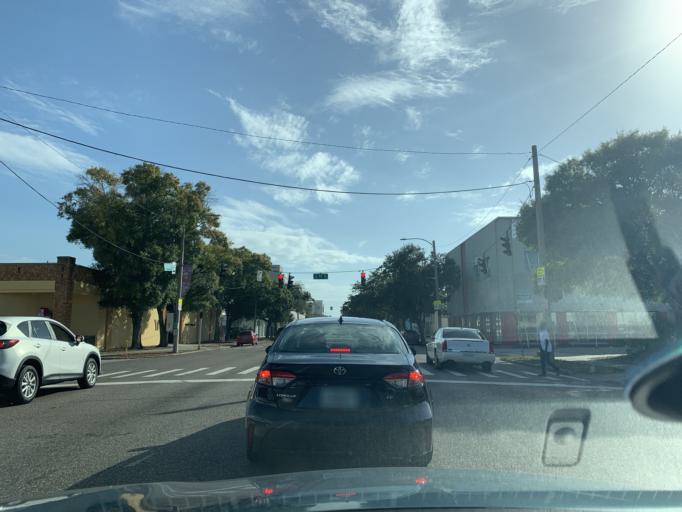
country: US
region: Florida
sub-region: Pinellas County
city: Saint Petersburg
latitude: 27.7755
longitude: -82.6467
